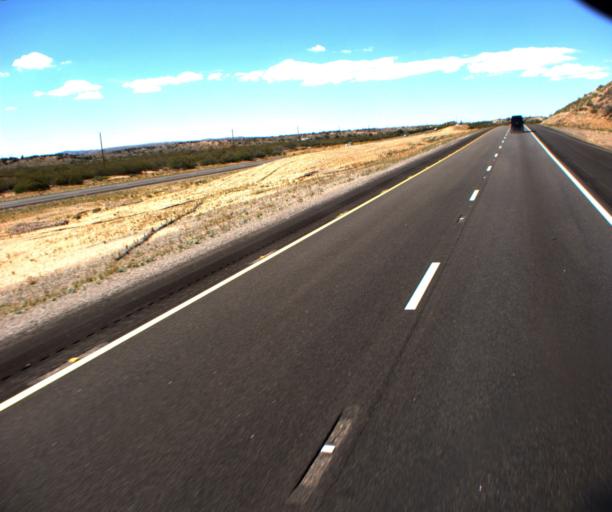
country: US
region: Arizona
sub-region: Mohave County
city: Kingman
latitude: 35.0173
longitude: -113.6640
